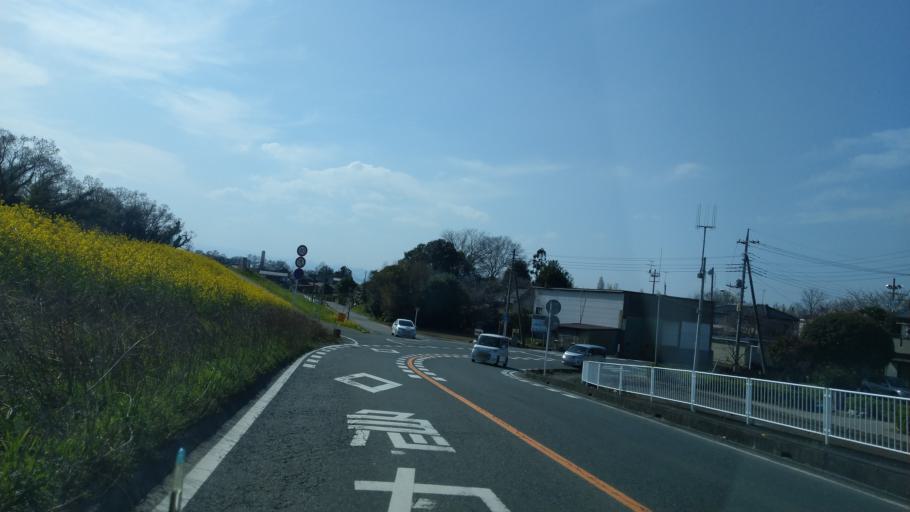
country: JP
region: Saitama
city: Okegawa
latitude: 35.9532
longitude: 139.5305
